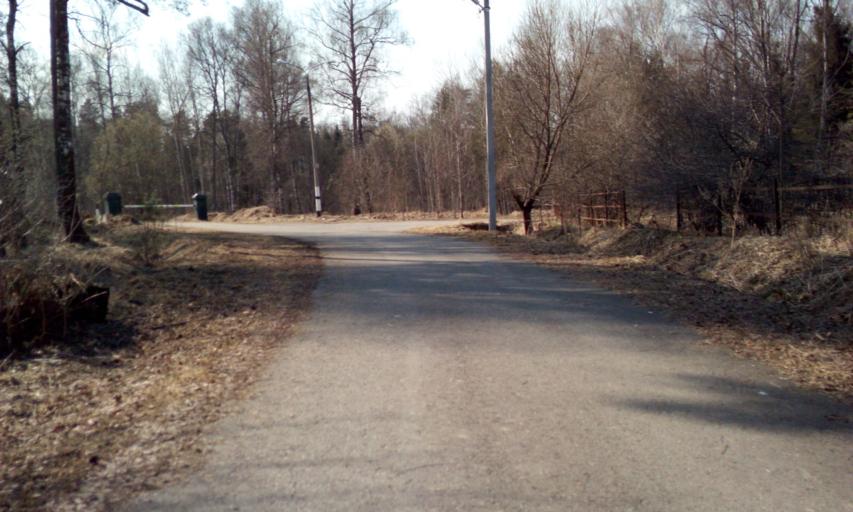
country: RU
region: Moskovskaya
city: Vatutinki
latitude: 55.4531
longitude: 37.3929
